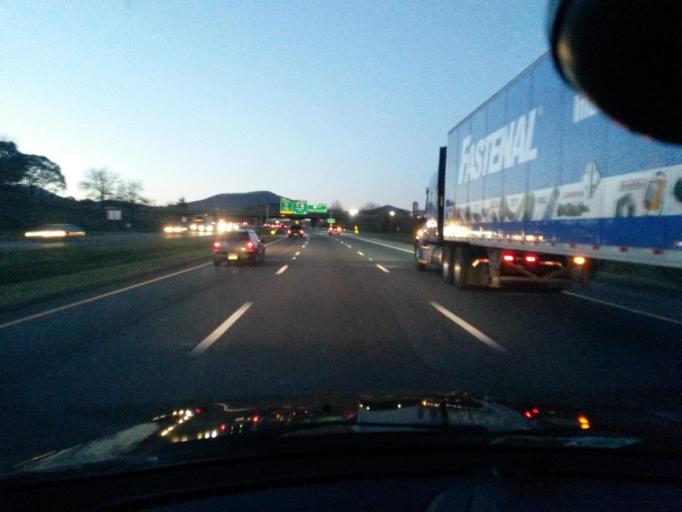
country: US
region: Virginia
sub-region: Roanoke County
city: Hollins
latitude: 37.3254
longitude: -79.9871
